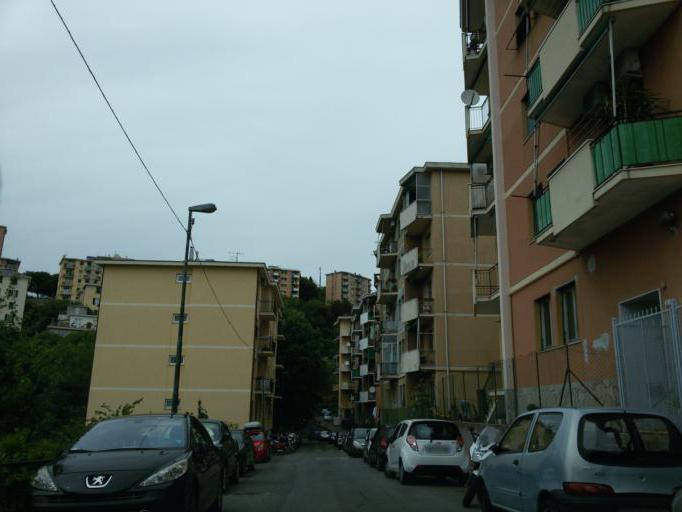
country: IT
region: Liguria
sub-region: Provincia di Genova
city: Genoa
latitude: 44.4259
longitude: 8.9293
